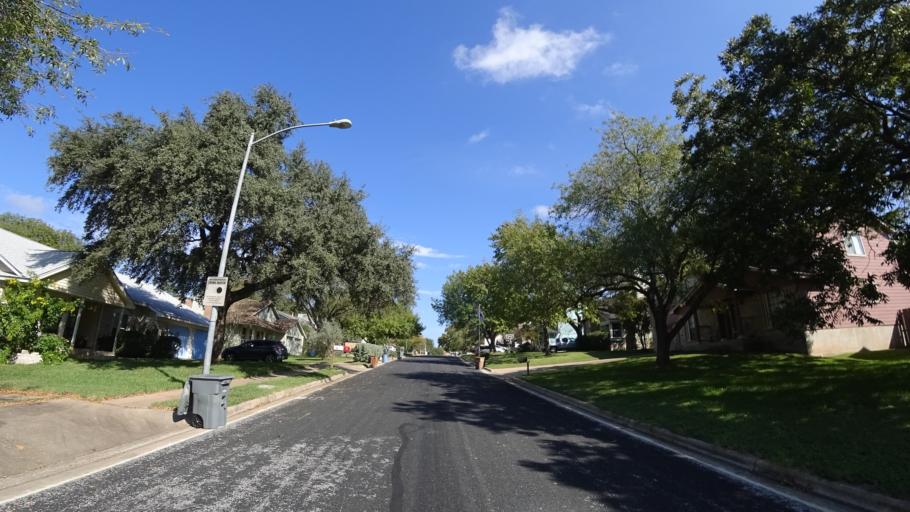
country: US
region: Texas
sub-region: Travis County
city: Shady Hollow
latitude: 30.1970
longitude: -97.8197
